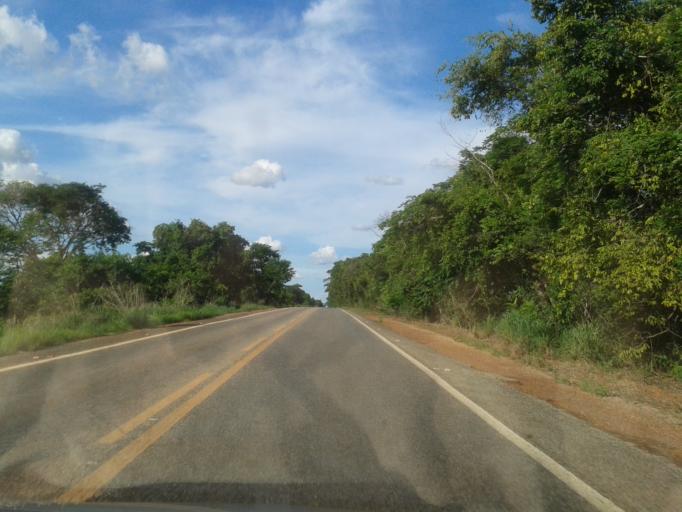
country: BR
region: Goias
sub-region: Mozarlandia
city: Mozarlandia
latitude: -14.4432
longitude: -50.4595
